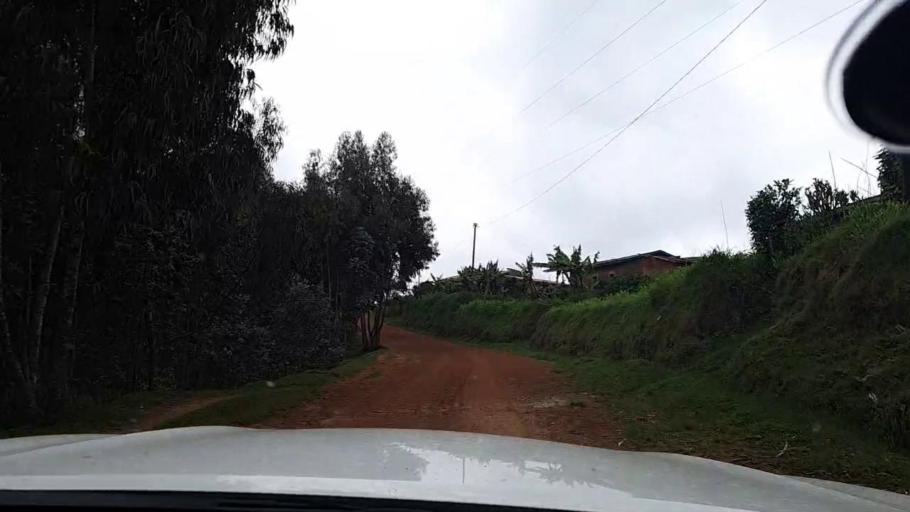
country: RW
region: Western Province
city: Kibuye
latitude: -2.1759
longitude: 29.4473
